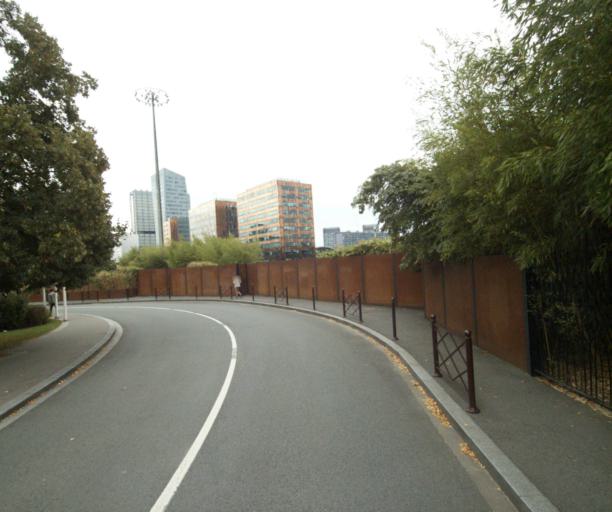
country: FR
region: Nord-Pas-de-Calais
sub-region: Departement du Nord
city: La Madeleine
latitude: 50.6421
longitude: 3.0753
